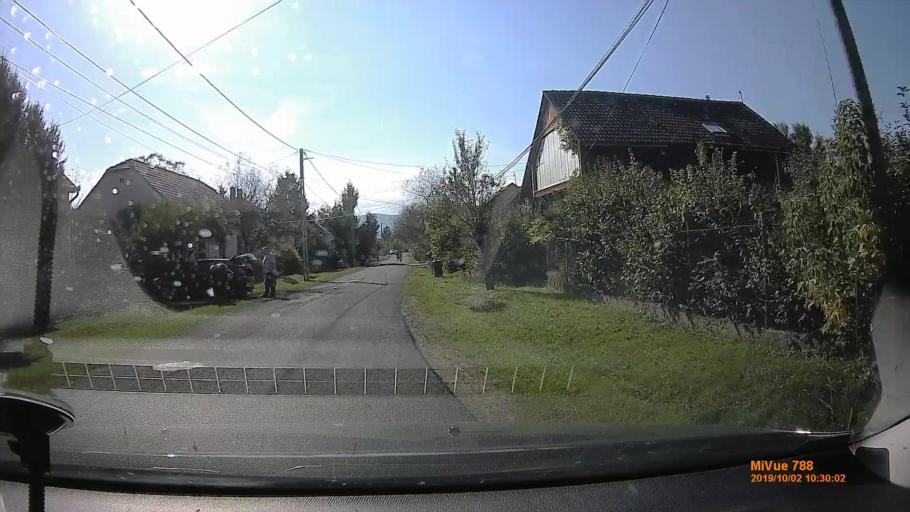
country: HU
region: Nograd
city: Kazar
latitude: 48.0192
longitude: 19.8259
